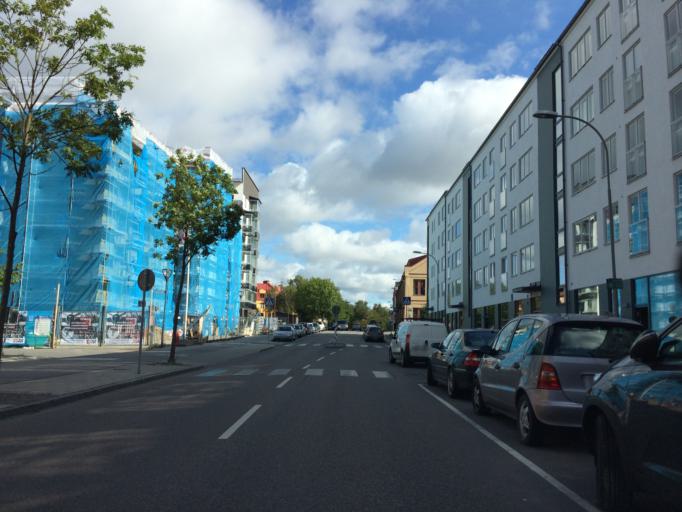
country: SE
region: Stockholm
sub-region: Stockholms Kommun
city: Arsta
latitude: 59.2977
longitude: 18.0018
